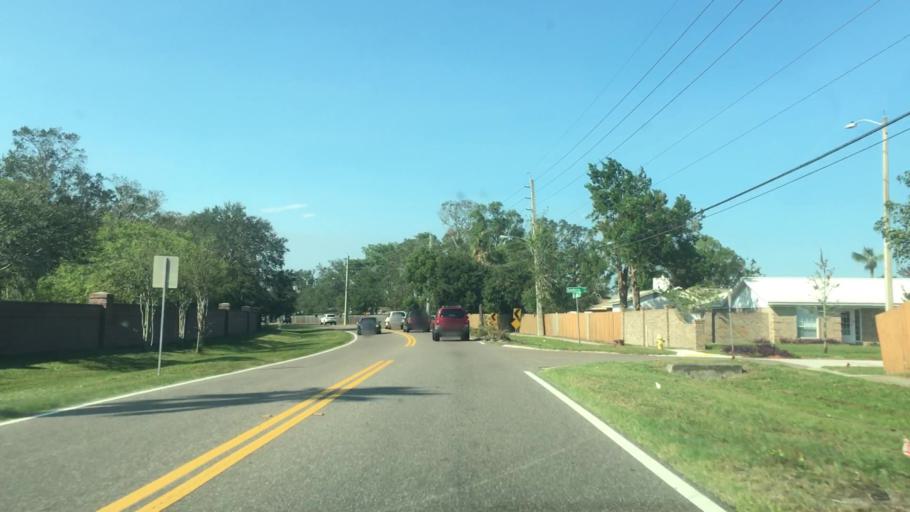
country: US
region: Florida
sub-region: Duval County
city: Neptune Beach
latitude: 30.2974
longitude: -81.4378
